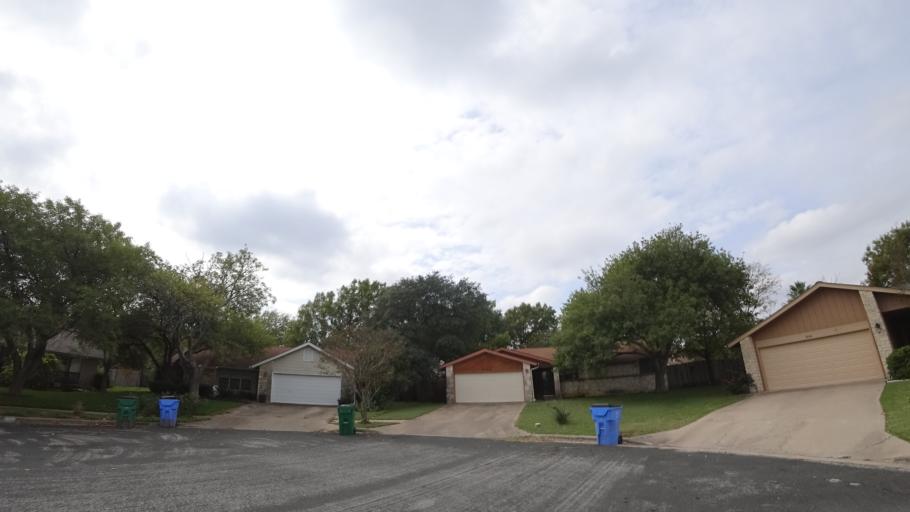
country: US
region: Texas
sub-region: Travis County
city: Wells Branch
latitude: 30.4395
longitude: -97.6831
